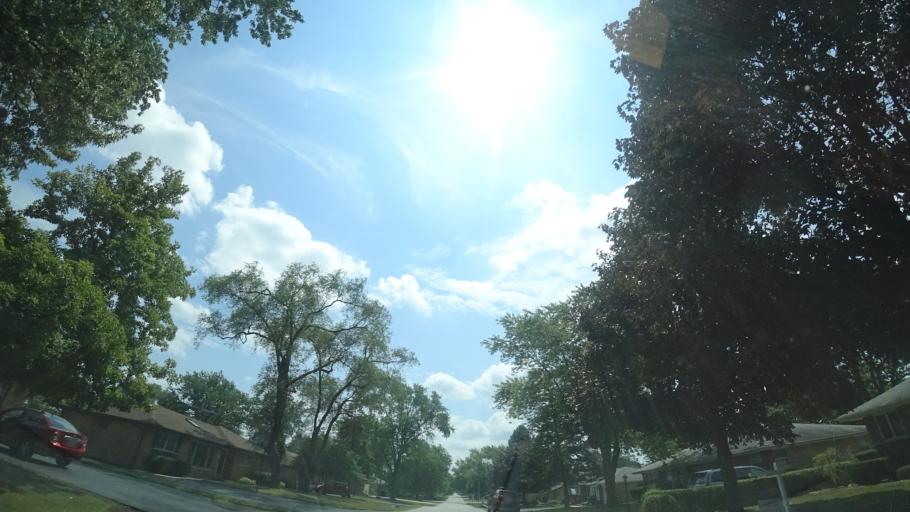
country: US
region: Illinois
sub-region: Cook County
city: Worth
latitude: 41.6859
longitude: -87.7823
